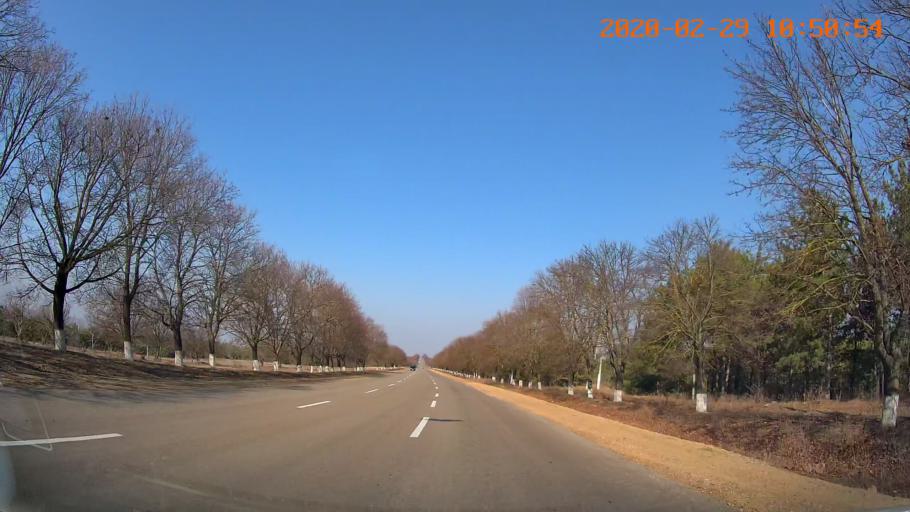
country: MD
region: Telenesti
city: Grigoriopol
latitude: 47.0877
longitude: 29.3710
